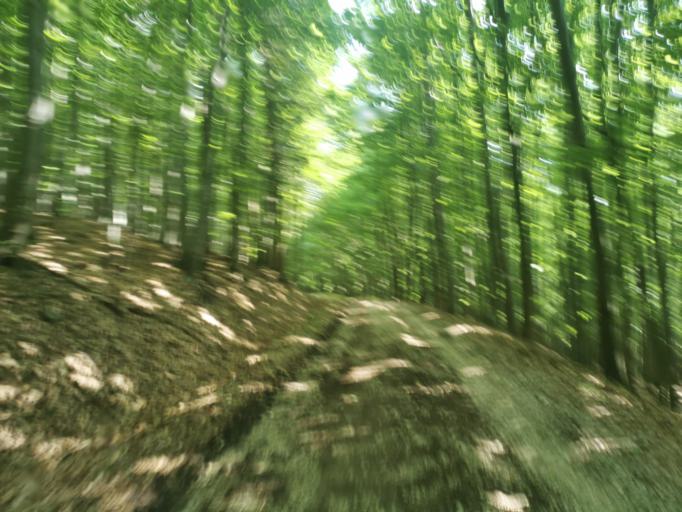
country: SK
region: Trenciansky
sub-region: Okres Myjava
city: Myjava
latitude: 48.8163
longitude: 17.5691
